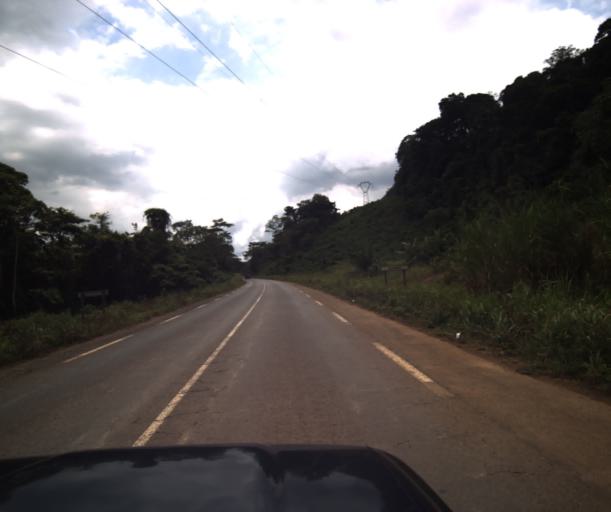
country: CM
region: Centre
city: Eseka
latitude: 3.8855
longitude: 10.7052
